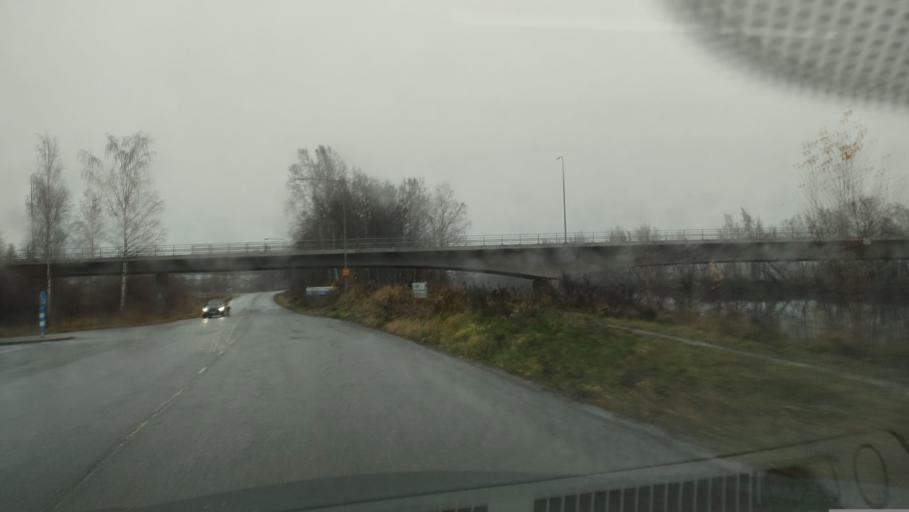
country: FI
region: Satakunta
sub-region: Pori
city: Pori
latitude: 61.5139
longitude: 21.7696
